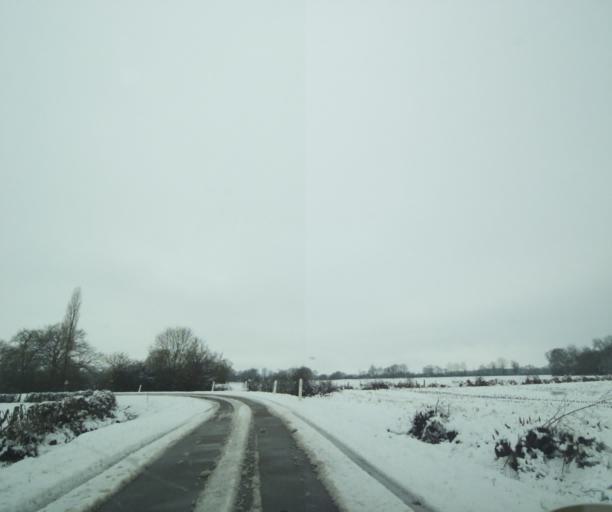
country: FR
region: Champagne-Ardenne
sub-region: Departement de la Haute-Marne
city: Montier-en-Der
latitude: 48.4706
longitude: 4.6602
